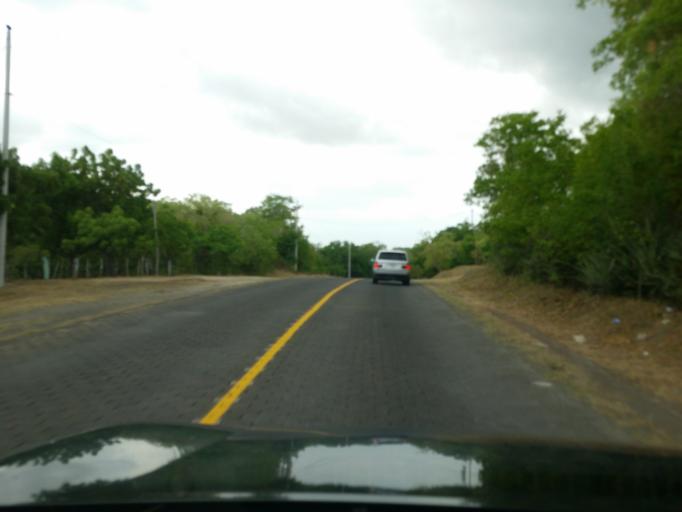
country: NI
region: Managua
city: Carlos Fonseca Amador
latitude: 11.9294
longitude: -86.5064
